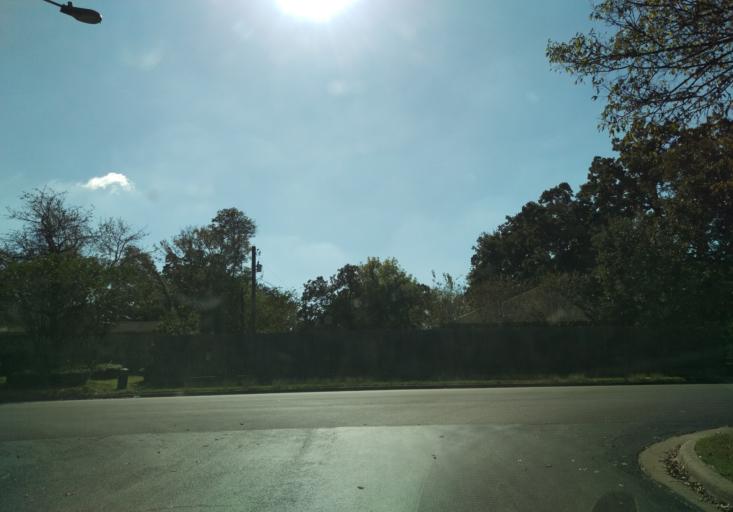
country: US
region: Texas
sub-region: Brazos County
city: College Station
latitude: 30.6197
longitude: -96.2869
